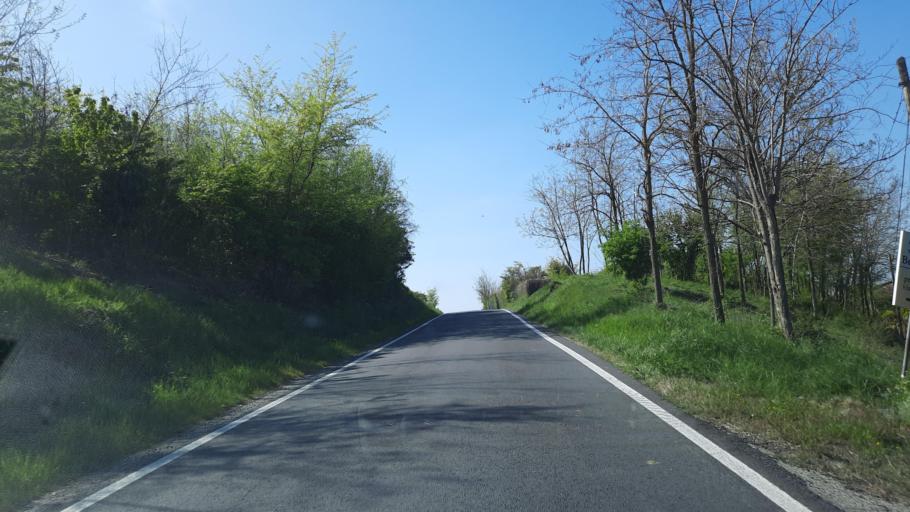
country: IT
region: Piedmont
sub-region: Provincia di Alessandria
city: Olivola
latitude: 45.0160
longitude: 8.3648
